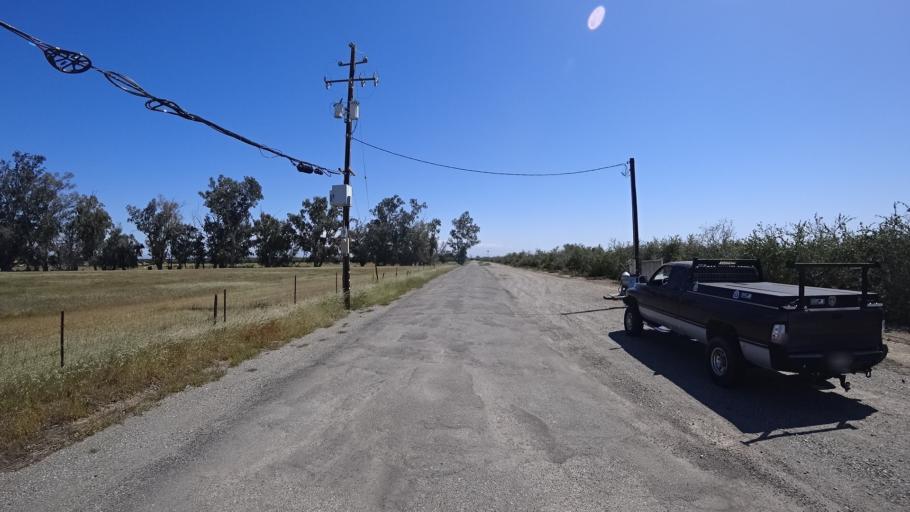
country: US
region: California
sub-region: Glenn County
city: Orland
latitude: 39.7215
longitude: -122.1407
